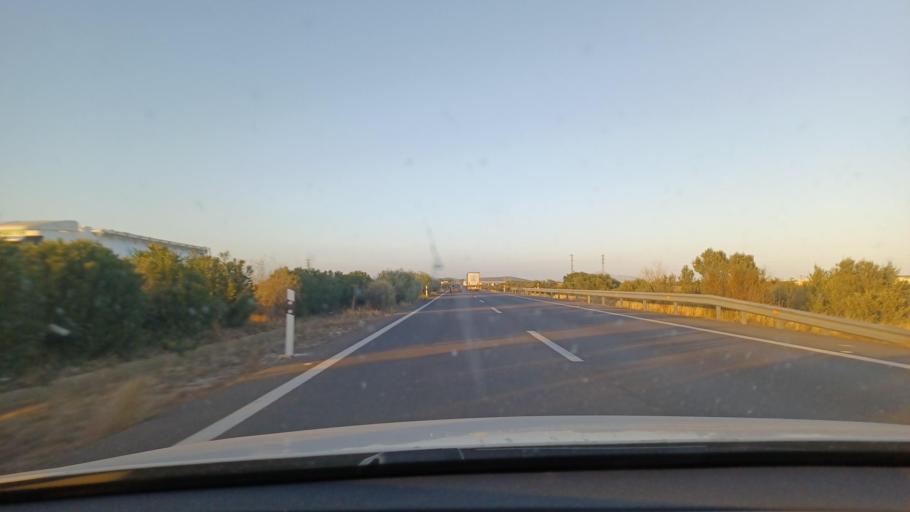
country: ES
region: Valencia
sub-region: Provincia de Castello
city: Benicarlo
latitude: 40.4327
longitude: 0.3872
